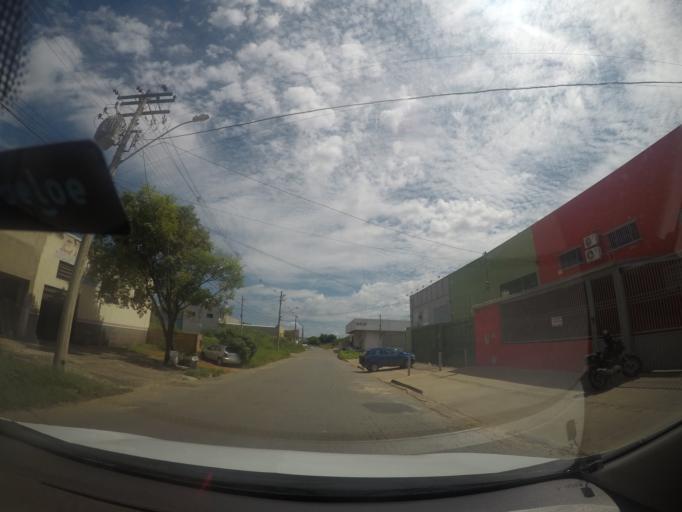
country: BR
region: Goias
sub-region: Goiania
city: Goiania
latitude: -16.6914
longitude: -49.3233
